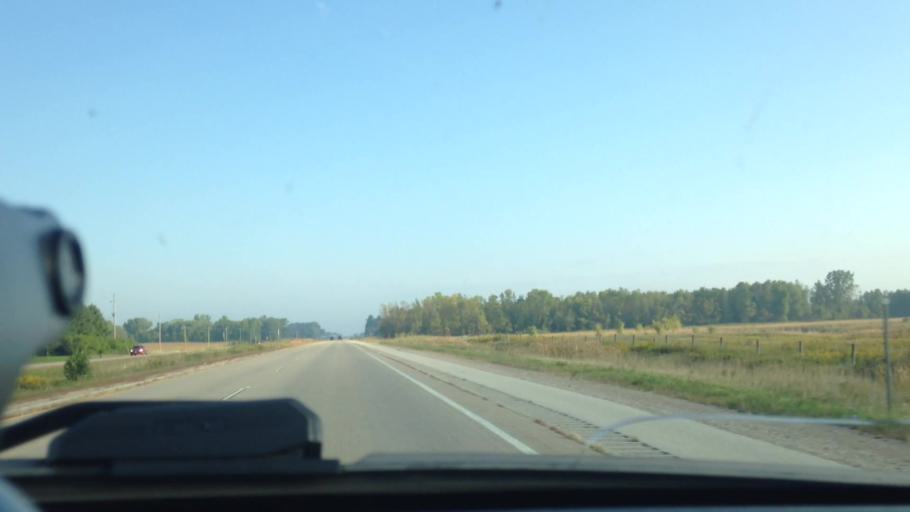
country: US
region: Wisconsin
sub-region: Oconto County
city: Oconto Falls
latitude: 45.0143
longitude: -88.0456
